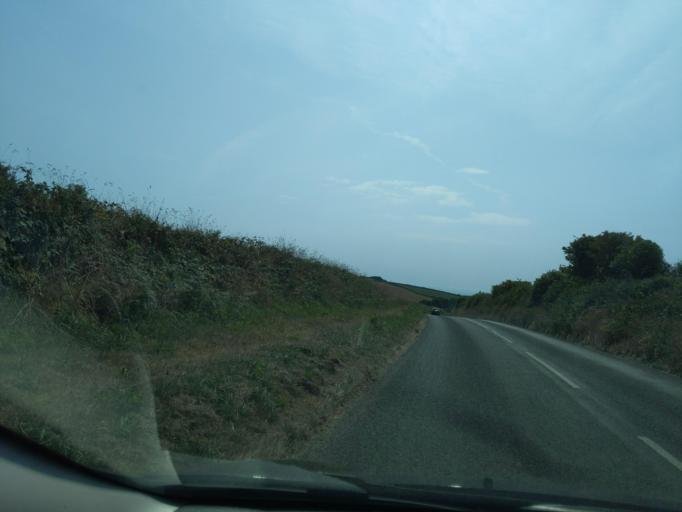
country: GB
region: England
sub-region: Cornwall
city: Fowey
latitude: 50.3498
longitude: -4.6133
